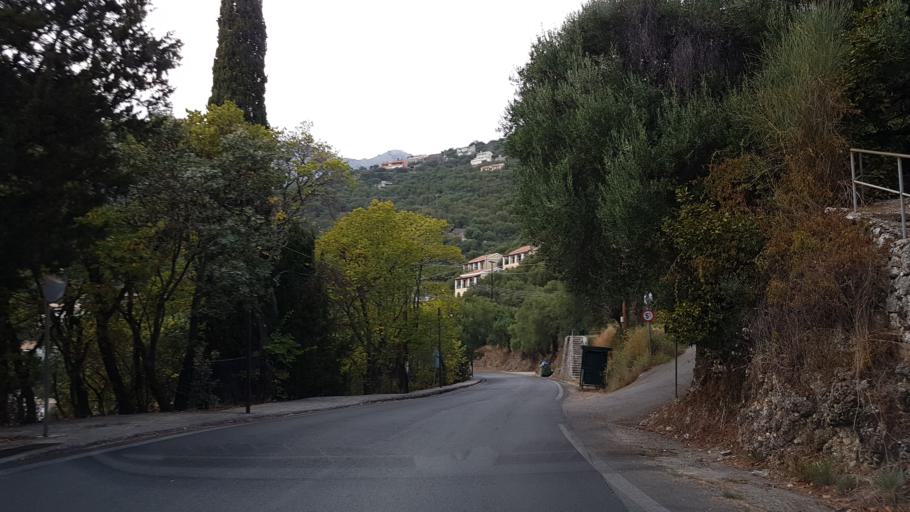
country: GR
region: Ionian Islands
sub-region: Nomos Kerkyras
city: Kontokali
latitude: 39.7260
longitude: 19.9005
